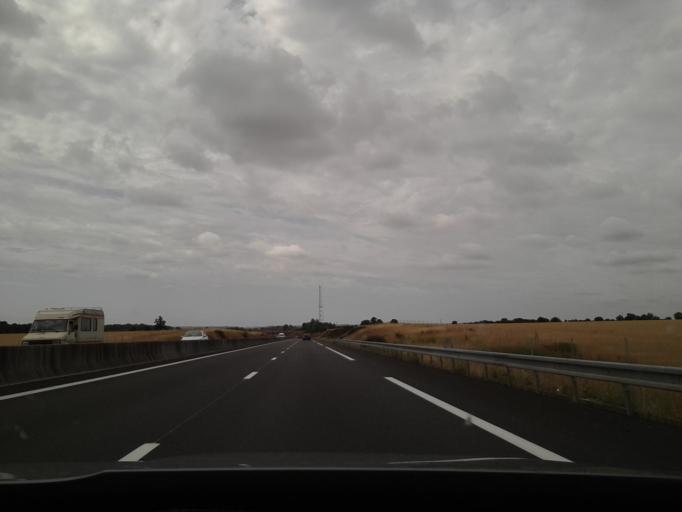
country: FR
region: Pays de la Loire
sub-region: Departement de la Sarthe
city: Arconnay
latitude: 48.3656
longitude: 0.1003
